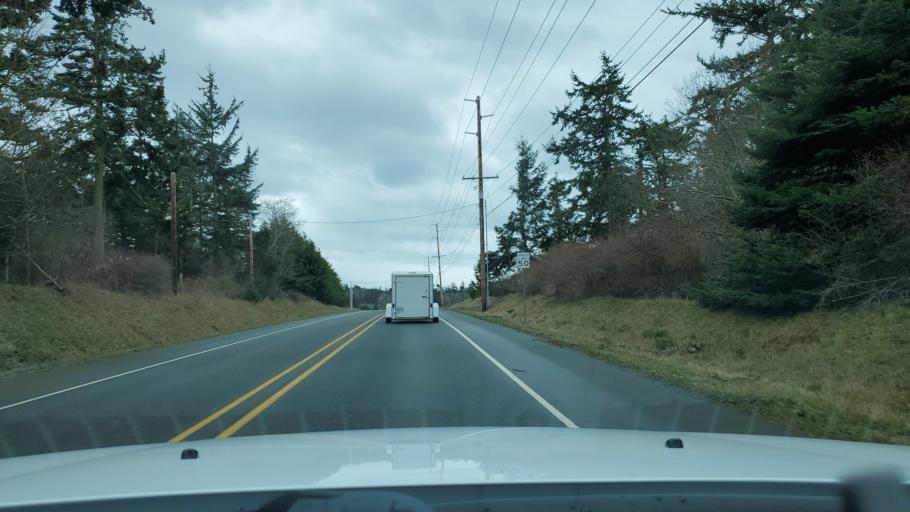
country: US
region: Washington
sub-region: Island County
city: Coupeville
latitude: 48.2525
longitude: -122.7516
